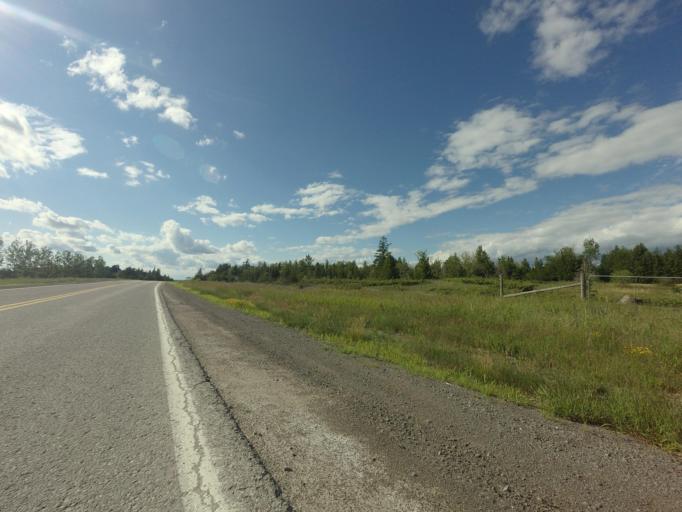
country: CA
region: Ontario
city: Arnprior
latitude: 45.3406
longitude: -76.1940
